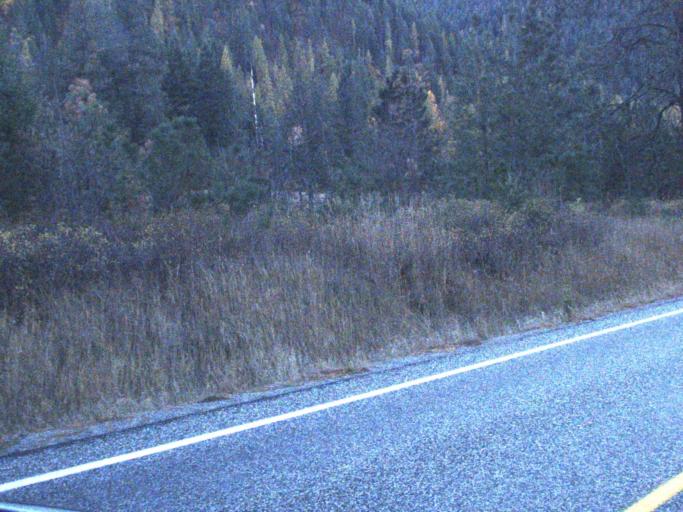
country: US
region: Washington
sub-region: Stevens County
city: Kettle Falls
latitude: 48.8108
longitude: -117.9415
